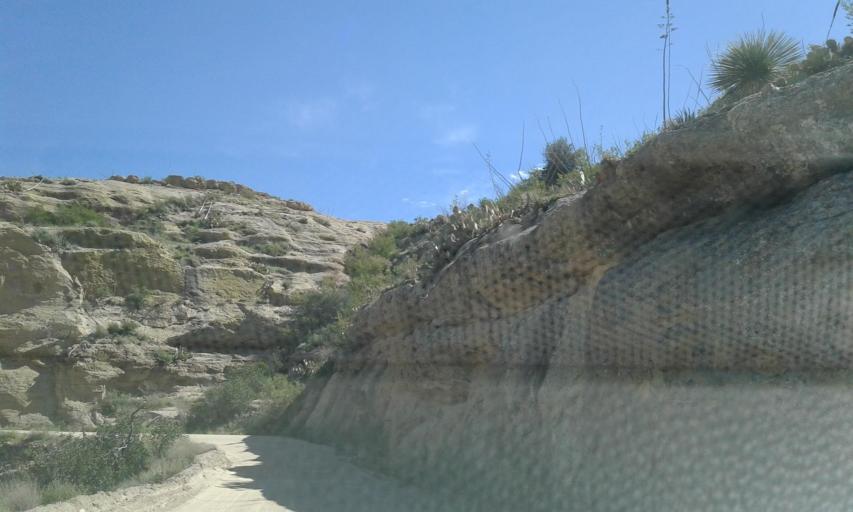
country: US
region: Arizona
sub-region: Pinal County
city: Gold Camp
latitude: 33.5302
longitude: -111.3150
